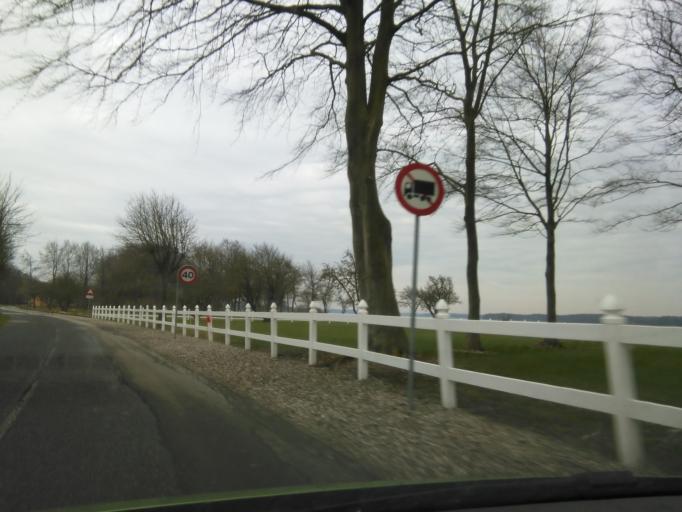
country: DK
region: North Denmark
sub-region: Mariagerfjord Kommune
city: Hadsund
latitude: 56.6885
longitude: 10.0493
